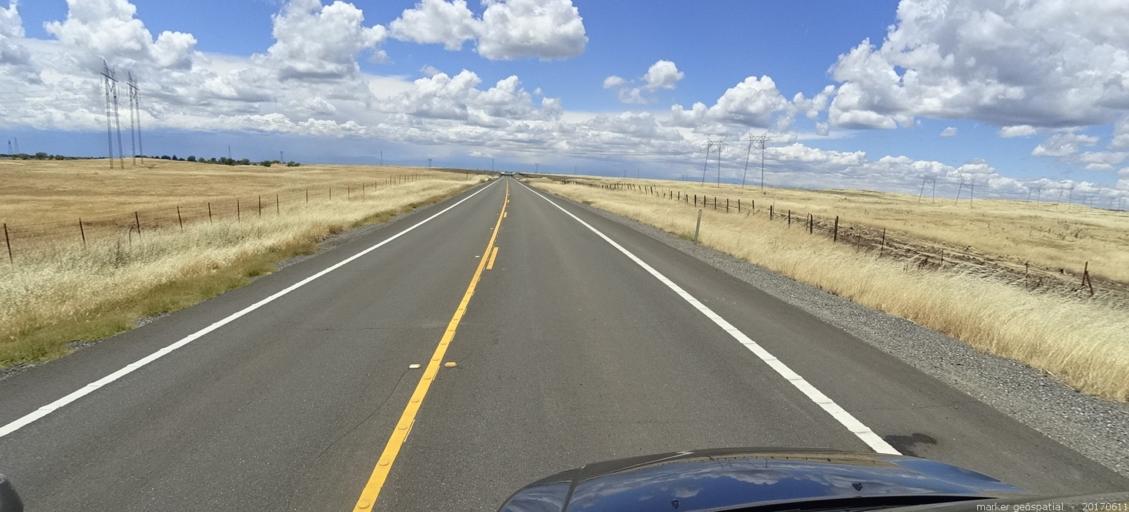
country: US
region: California
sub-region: Butte County
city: Durham
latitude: 39.6394
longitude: -121.6868
